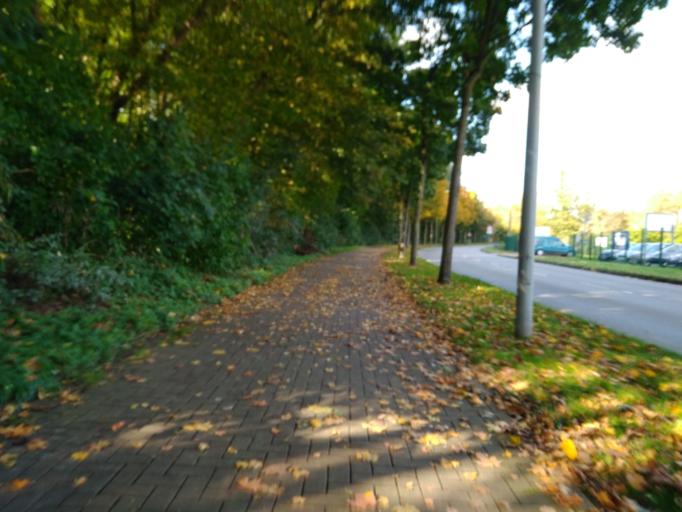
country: DE
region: North Rhine-Westphalia
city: Dorsten
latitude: 51.6087
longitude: 6.9318
